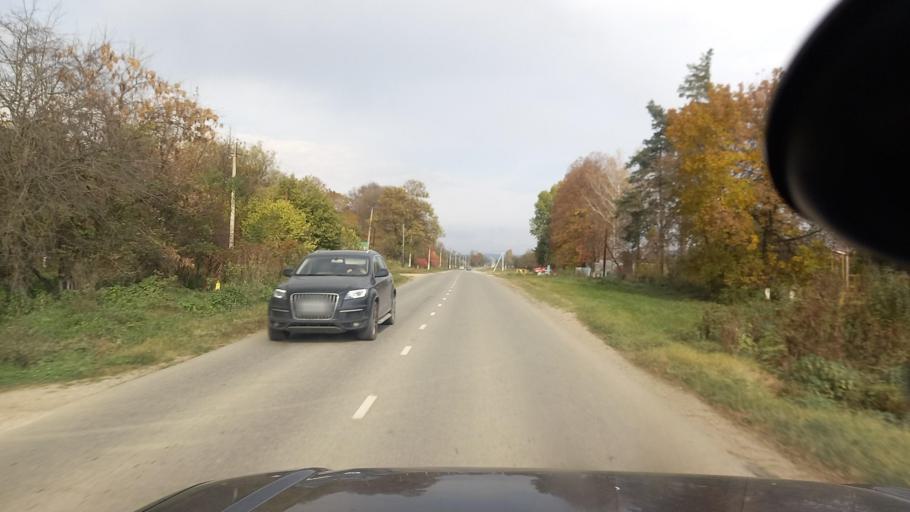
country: RU
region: Krasnodarskiy
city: Psebay
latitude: 44.1337
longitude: 40.8139
